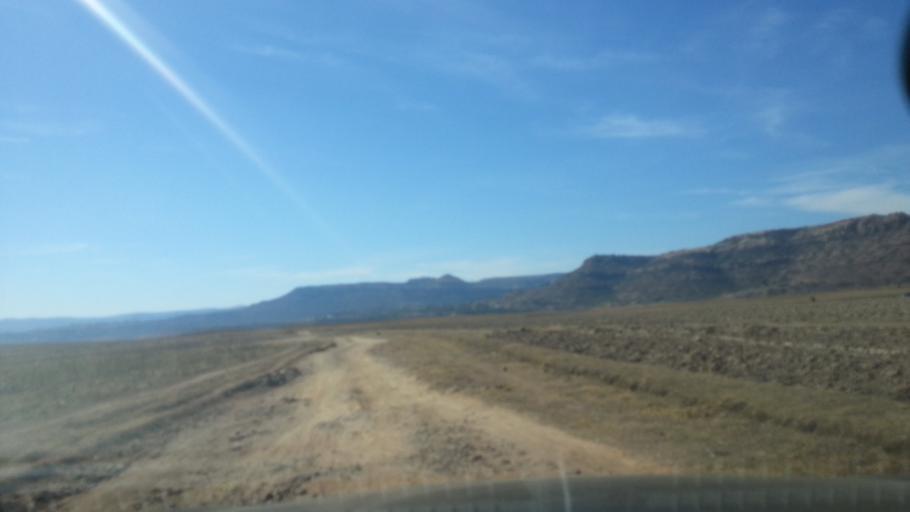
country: LS
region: Maseru
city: Nako
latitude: -29.5118
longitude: 27.6149
